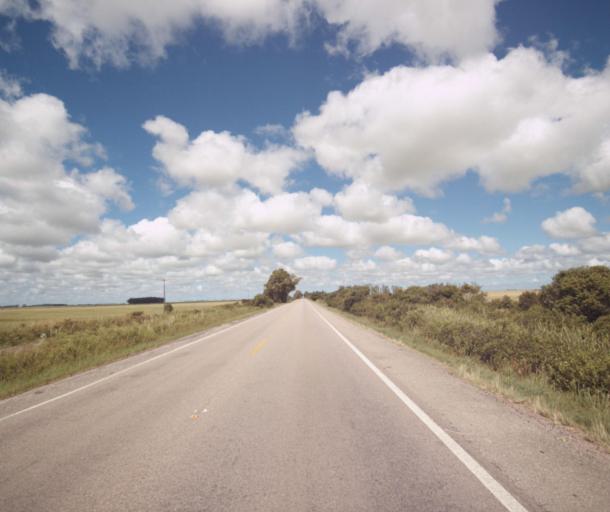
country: BR
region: Rio Grande do Sul
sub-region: Rio Grande
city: Rio Grande
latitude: -32.1769
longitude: -52.4191
